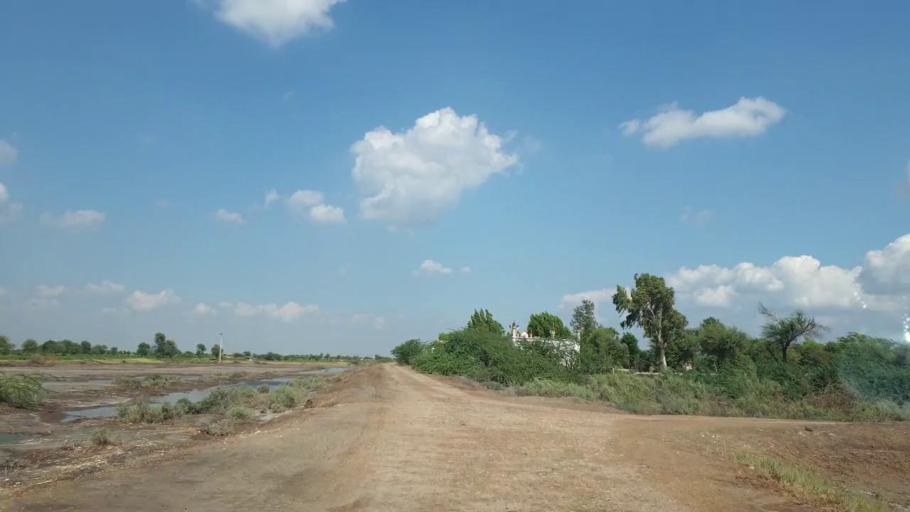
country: PK
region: Sindh
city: Pithoro
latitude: 25.6002
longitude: 69.3920
